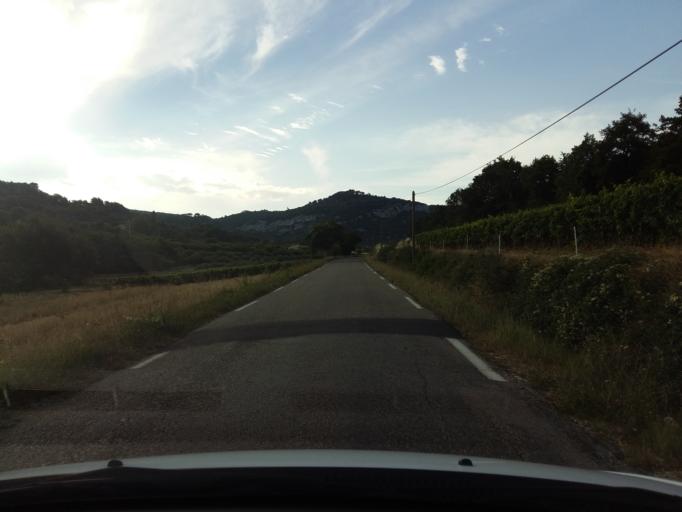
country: FR
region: Provence-Alpes-Cote d'Azur
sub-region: Departement du Vaucluse
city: Venasque
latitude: 43.9891
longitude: 5.1694
